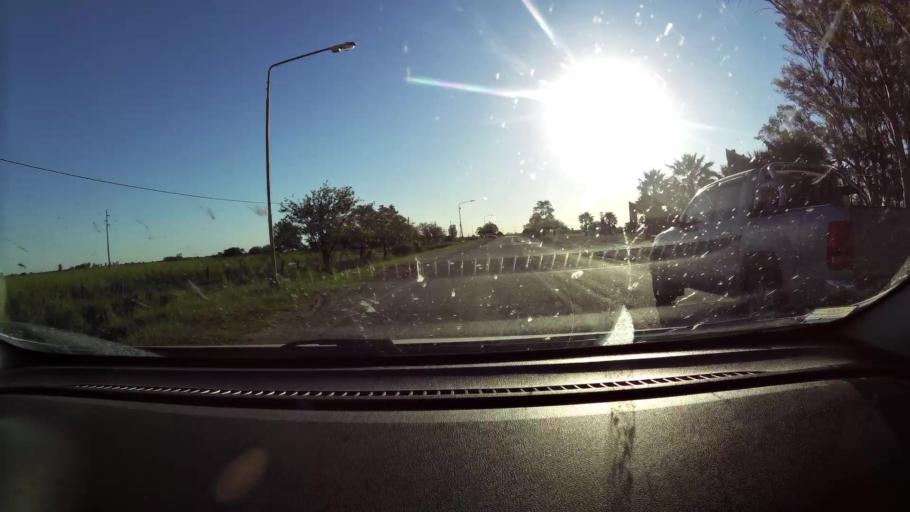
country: AR
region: Cordoba
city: Saturnino M. Laspiur
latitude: -31.7084
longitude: -62.4901
